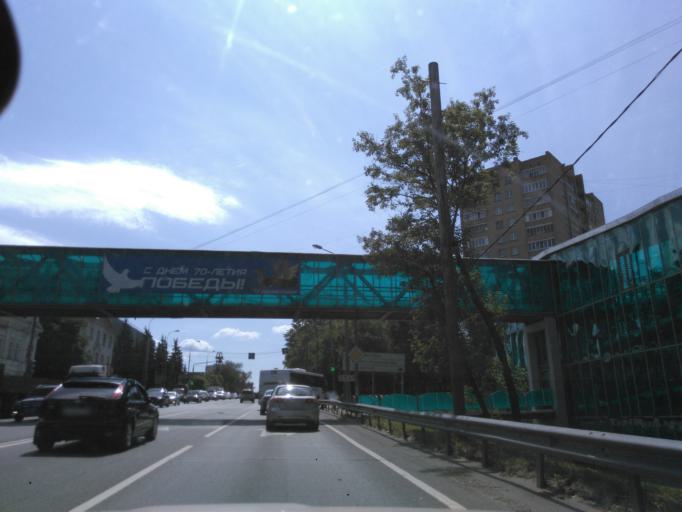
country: RU
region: Moskovskaya
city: Solnechnogorsk
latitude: 56.1897
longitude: 36.9740
